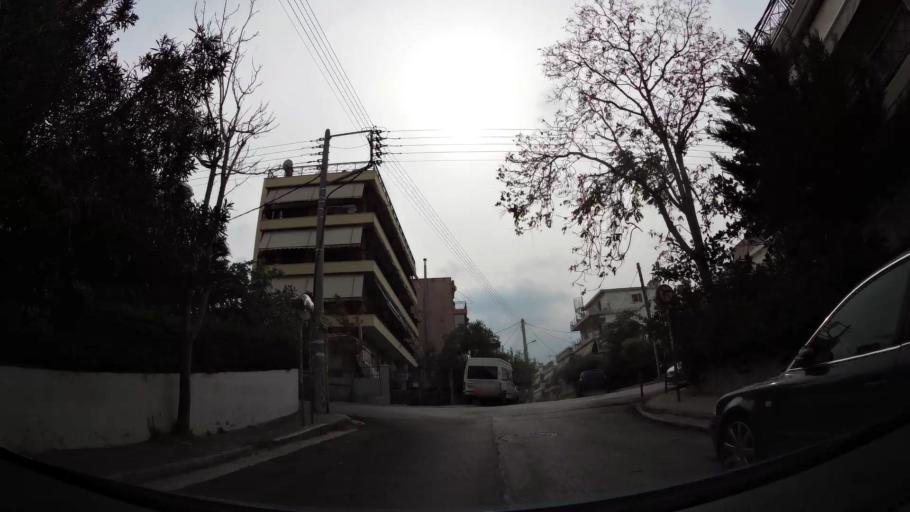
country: GR
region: Attica
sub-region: Nomarchia Athinas
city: Alimos
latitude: 37.9204
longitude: 23.7290
